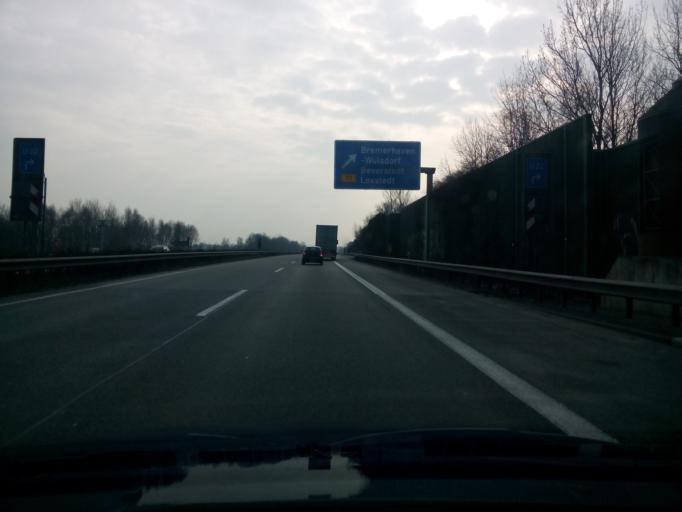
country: DE
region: Lower Saxony
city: Loxstedt
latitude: 53.4987
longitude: 8.6273
